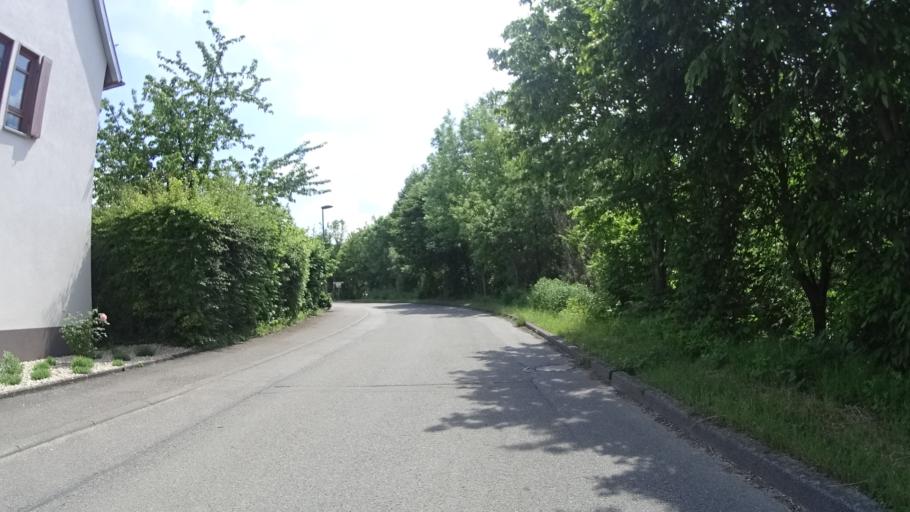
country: DE
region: Baden-Wuerttemberg
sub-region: Freiburg Region
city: Weisweil
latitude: 48.1950
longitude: 7.6727
